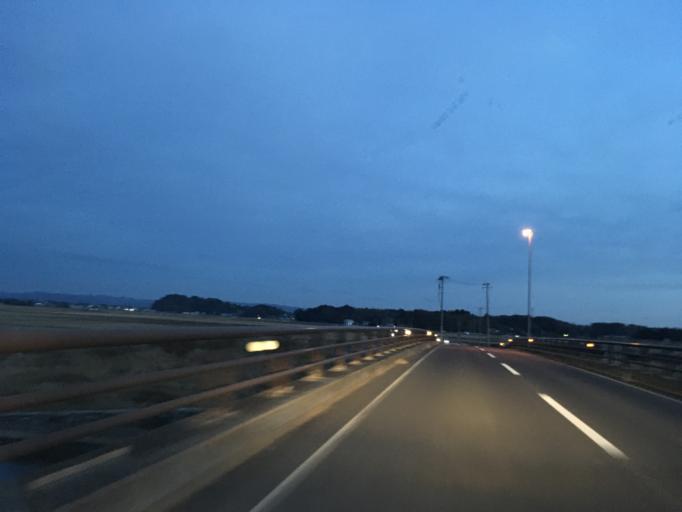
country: JP
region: Miyagi
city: Wakuya
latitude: 38.7119
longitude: 141.1480
